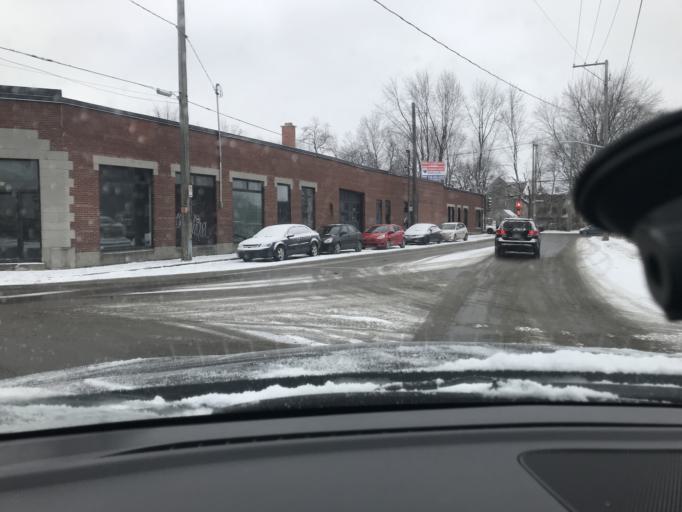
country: CA
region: Quebec
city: Quebec
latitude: 46.8164
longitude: -71.2287
